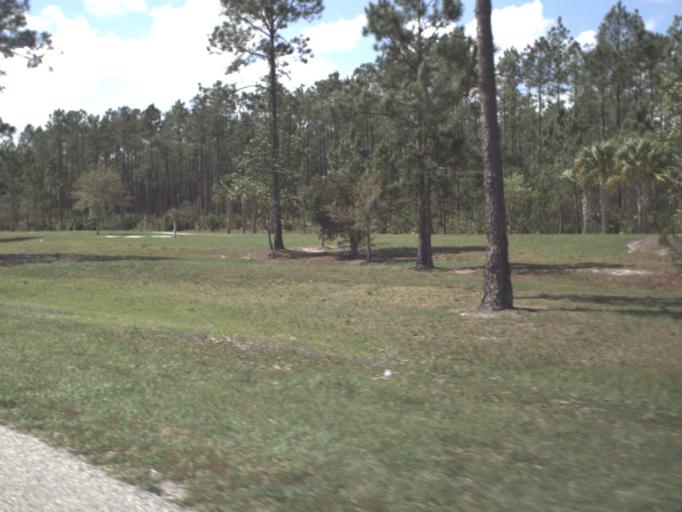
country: US
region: Florida
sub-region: Flagler County
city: Palm Coast
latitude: 29.5753
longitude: -81.2760
